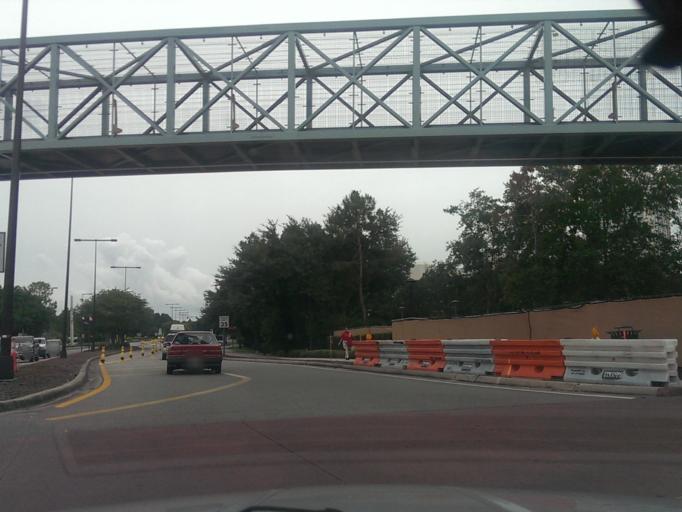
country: US
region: Florida
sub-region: Osceola County
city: Celebration
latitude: 28.3733
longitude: -81.5131
